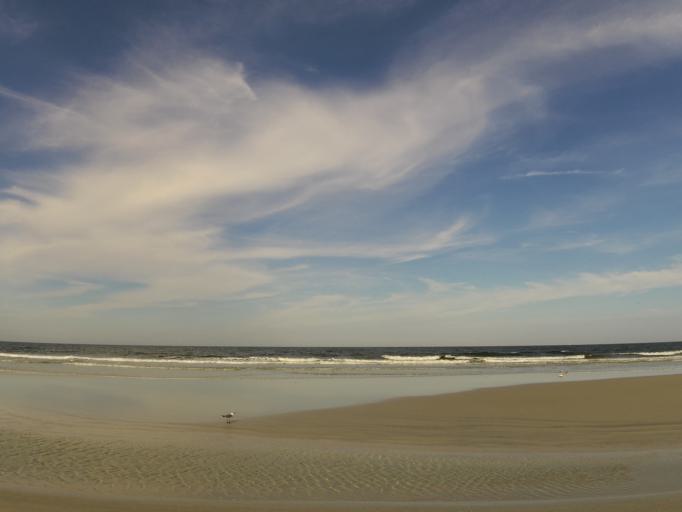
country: US
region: Florida
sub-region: Duval County
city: Atlantic Beach
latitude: 30.4450
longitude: -81.4091
